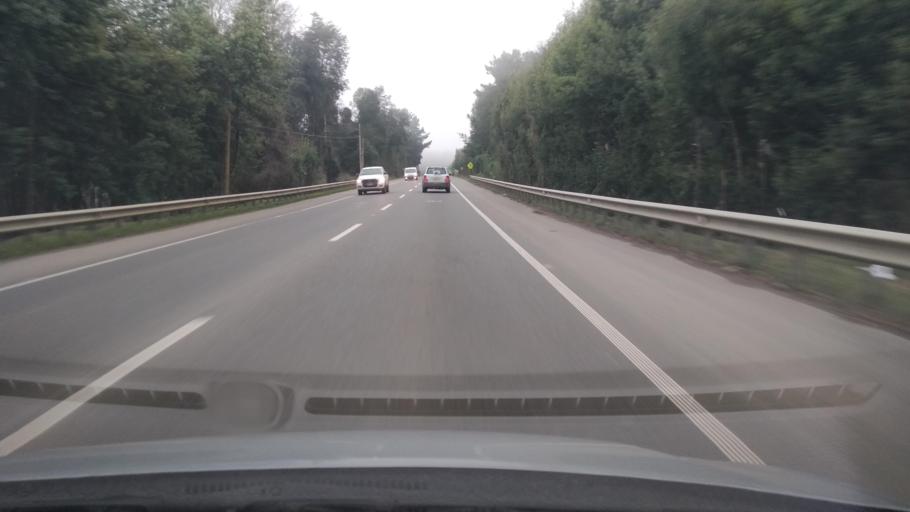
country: CL
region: Los Lagos
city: Las Animas
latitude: -39.7319
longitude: -73.2045
